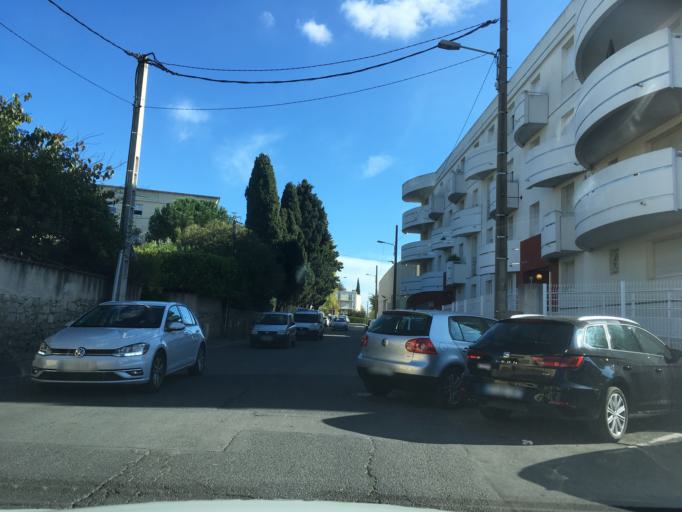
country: FR
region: Languedoc-Roussillon
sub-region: Departement de l'Herault
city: Juvignac
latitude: 43.6114
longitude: 3.8314
